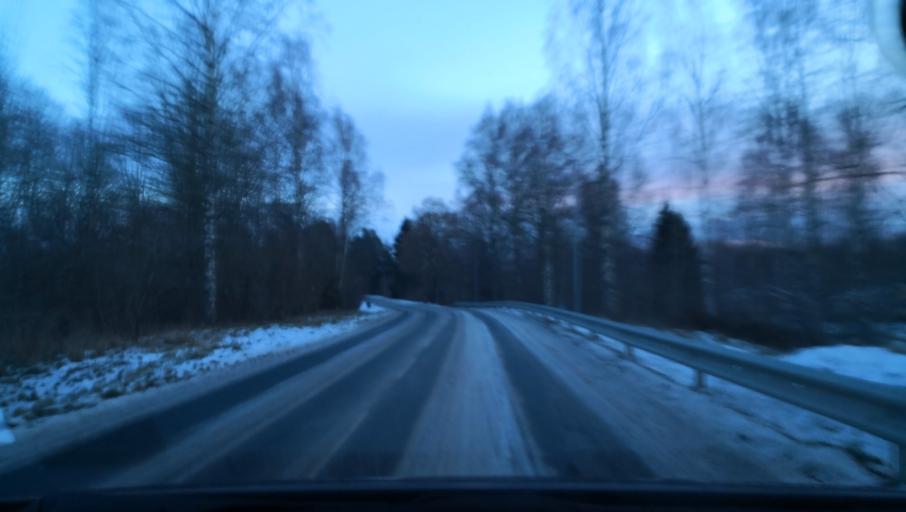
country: SE
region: Soedermanland
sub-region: Katrineholms Kommun
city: Katrineholm
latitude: 59.0869
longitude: 16.2161
